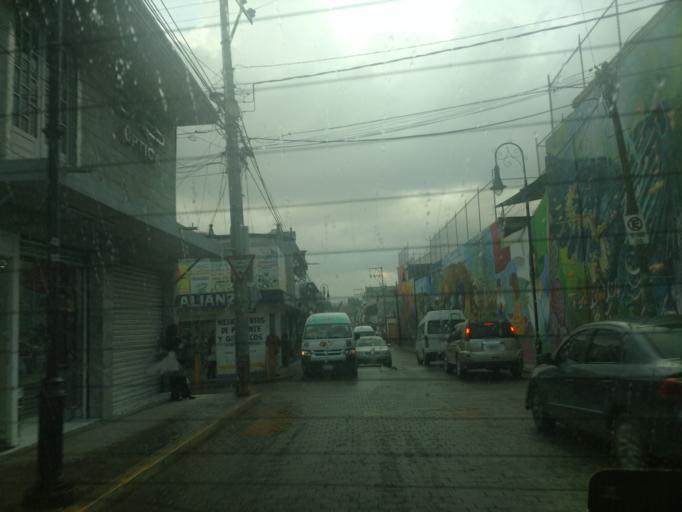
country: MX
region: Morelos
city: Coyotepec
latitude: 19.7756
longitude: -99.2088
